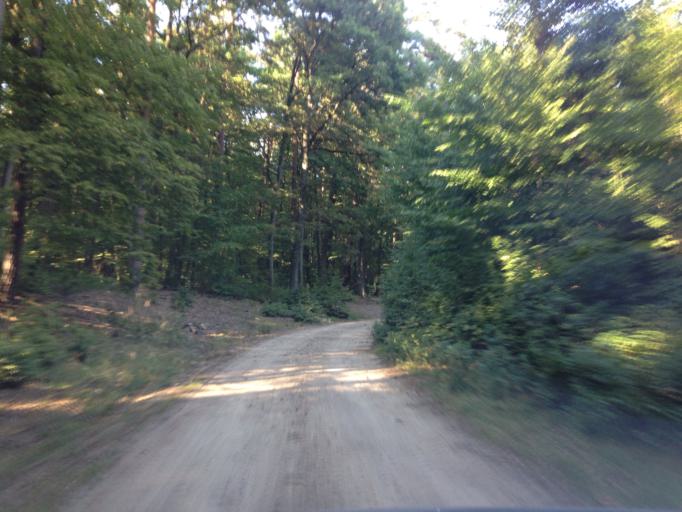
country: PL
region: Kujawsko-Pomorskie
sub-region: Powiat brodnicki
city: Gorzno
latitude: 53.1843
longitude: 19.6774
